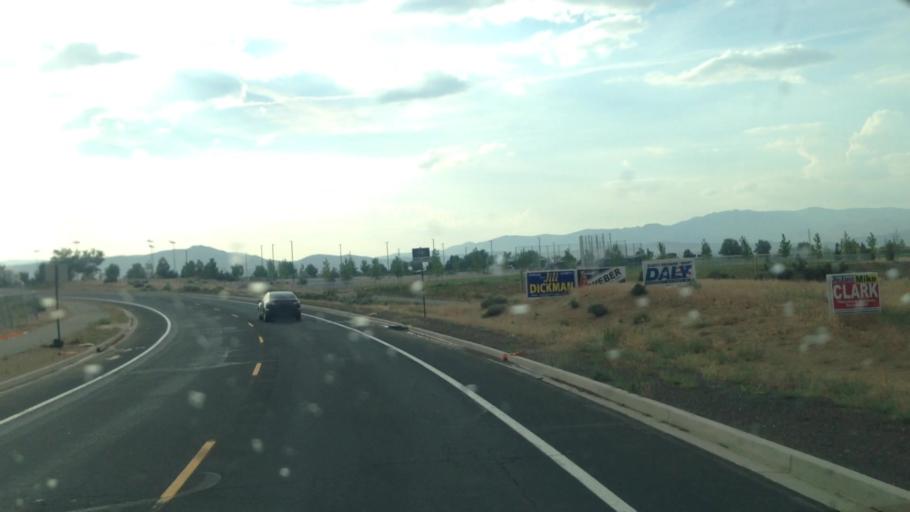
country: US
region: Nevada
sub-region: Washoe County
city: Lemmon Valley
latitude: 39.6209
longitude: -119.8617
